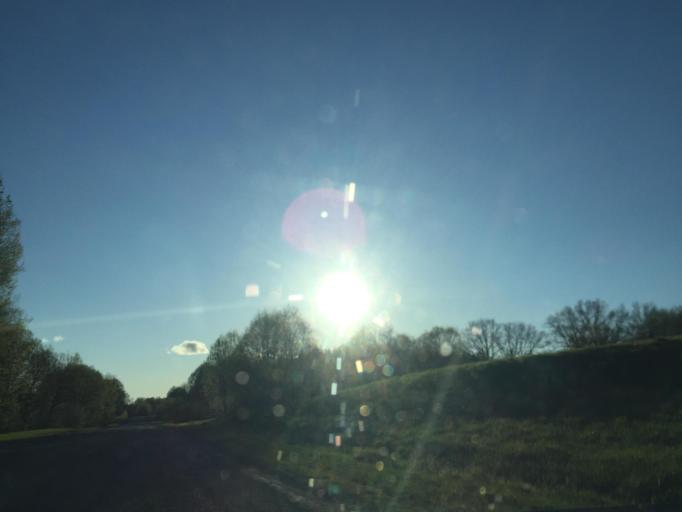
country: LV
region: Vecpiebalga
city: Vecpiebalga
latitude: 56.8414
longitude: 25.9510
